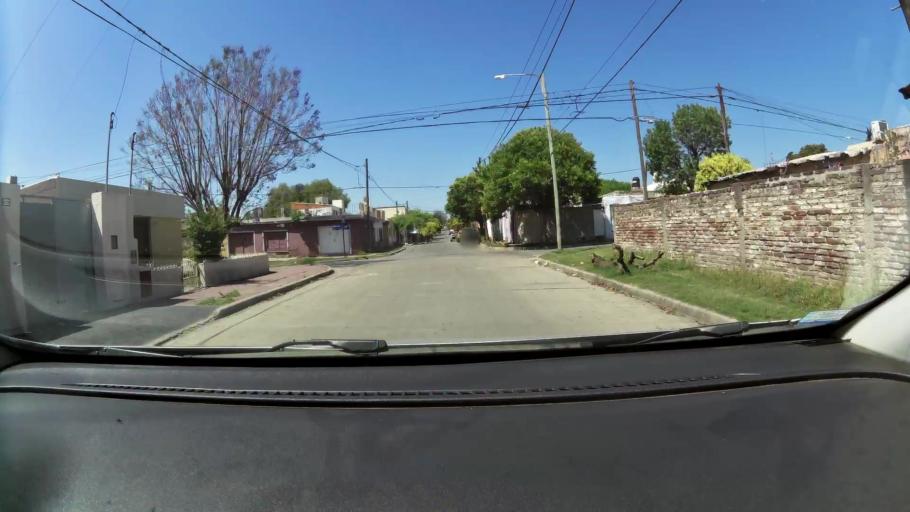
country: AR
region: Cordoba
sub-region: Departamento de Capital
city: Cordoba
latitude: -31.4182
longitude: -64.2066
